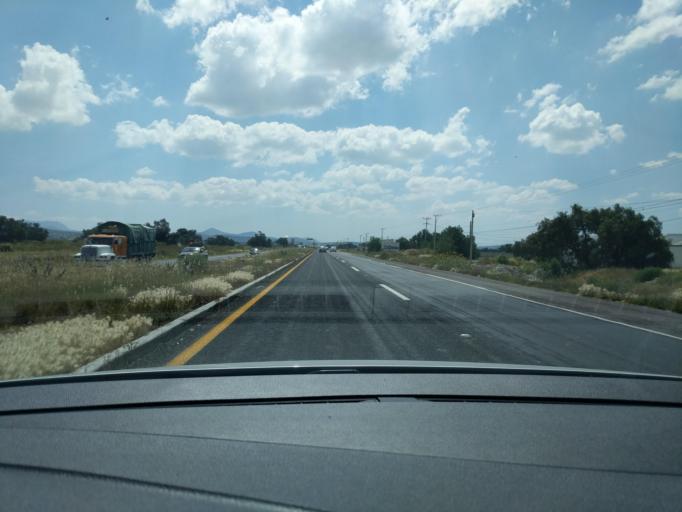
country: MX
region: Hidalgo
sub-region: Mineral de la Reforma
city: Rinconada de los Angeles
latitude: 19.9805
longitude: -98.7023
